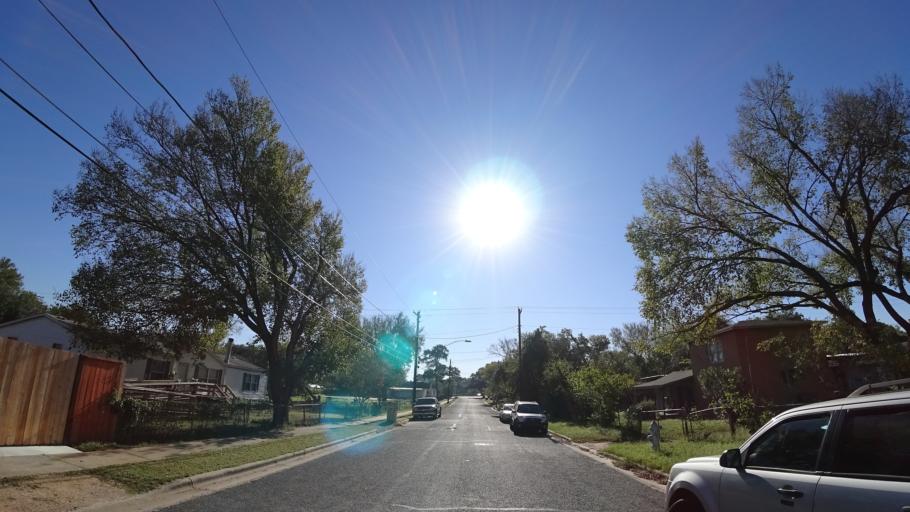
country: US
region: Texas
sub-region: Travis County
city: Austin
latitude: 30.2370
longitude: -97.6978
